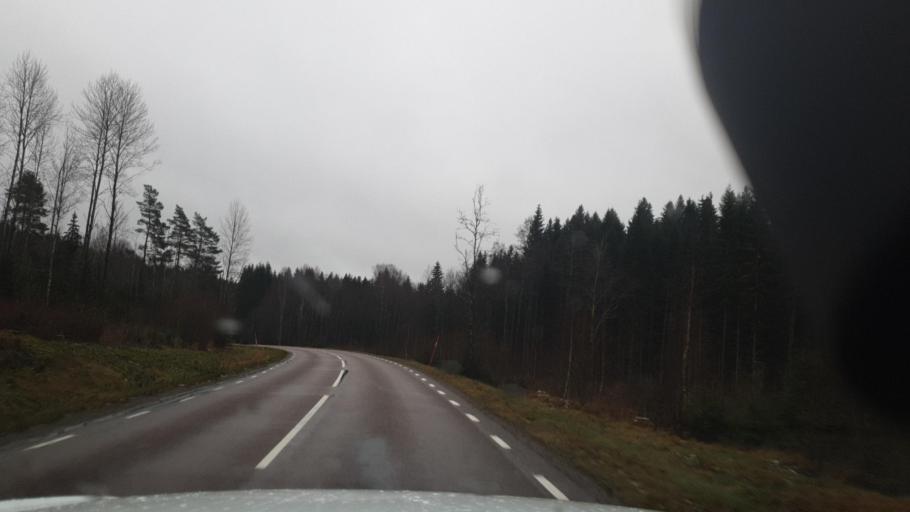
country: SE
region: Vaermland
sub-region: Grums Kommun
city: Slottsbron
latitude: 59.4514
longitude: 12.8457
